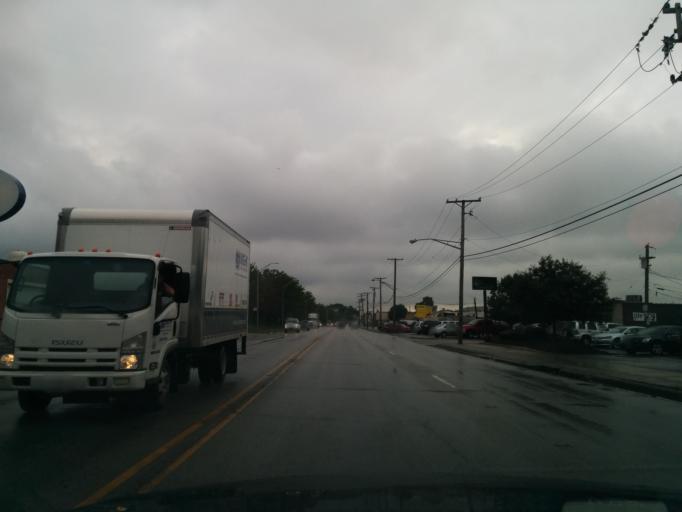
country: US
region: Illinois
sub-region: Cook County
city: Stone Park
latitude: 41.8981
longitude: -87.8880
